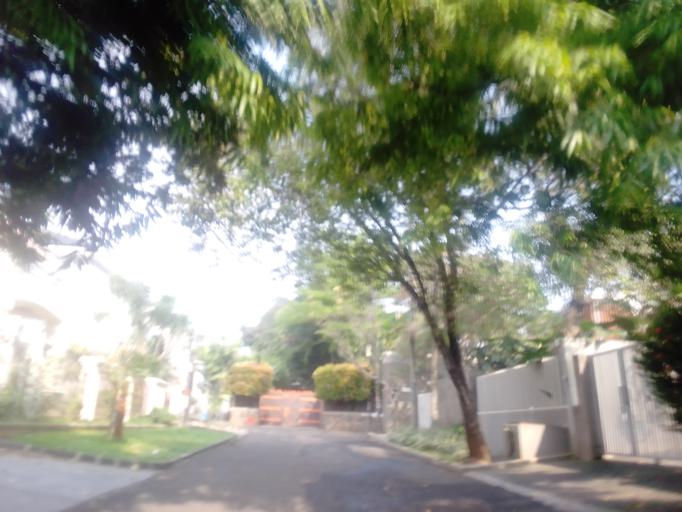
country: ID
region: Jakarta Raya
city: Jakarta
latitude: -6.2570
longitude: 106.7987
